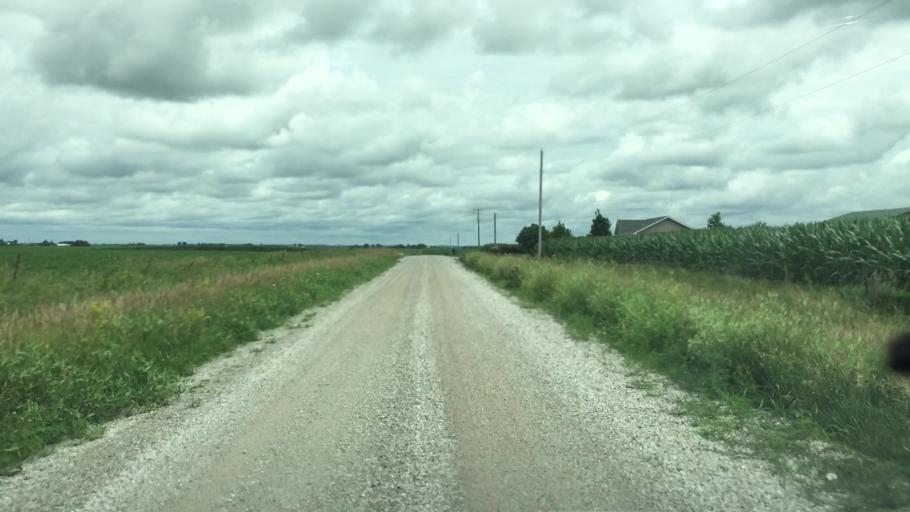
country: US
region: Iowa
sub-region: Jasper County
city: Monroe
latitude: 41.5745
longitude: -93.1208
